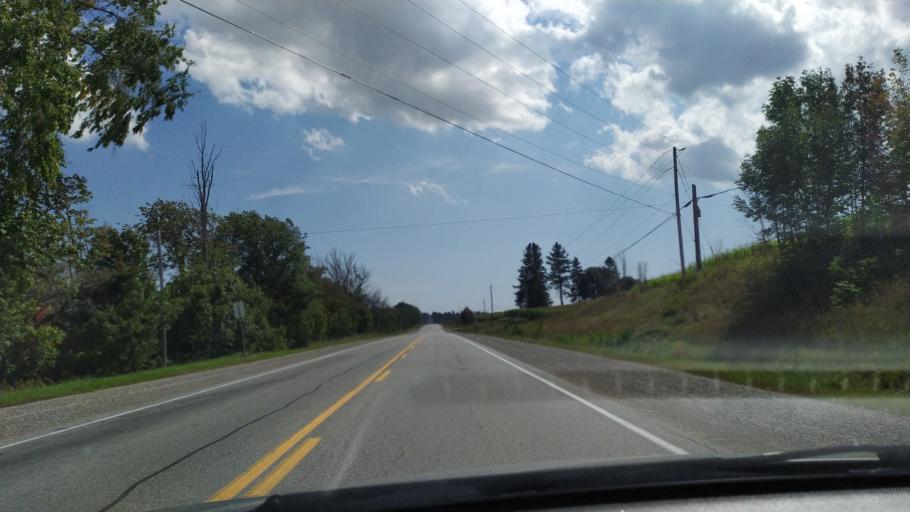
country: CA
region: Ontario
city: Ingersoll
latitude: 43.1490
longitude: -80.8978
